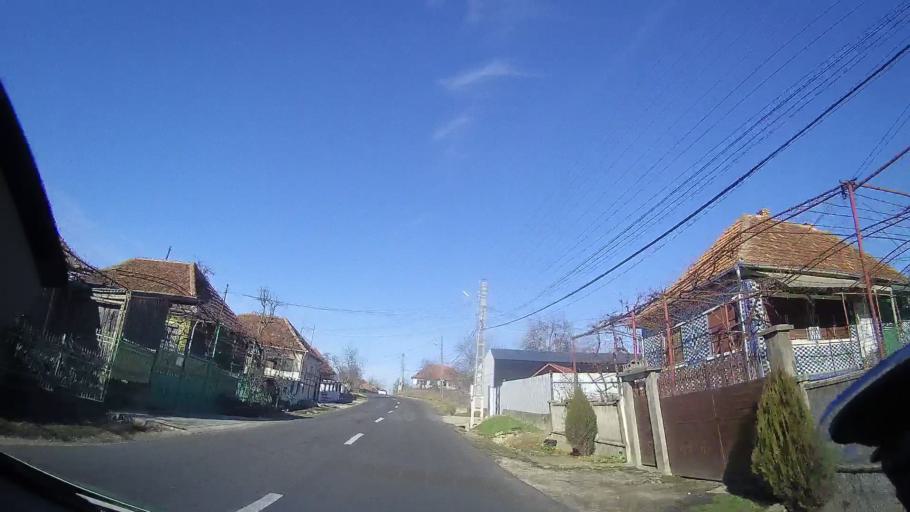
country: RO
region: Bihor
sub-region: Comuna Bratca
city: Beznea
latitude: 46.9680
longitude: 22.6144
